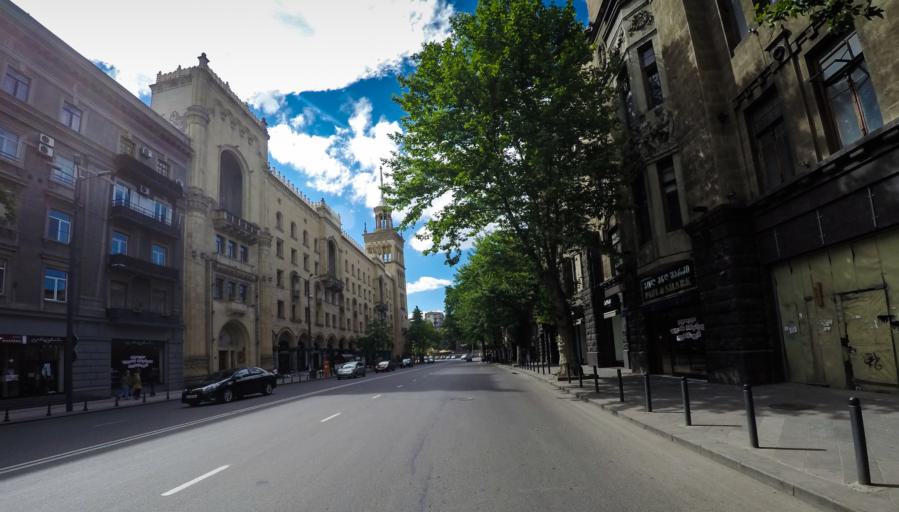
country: GE
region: T'bilisi
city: Tbilisi
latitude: 41.7031
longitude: 44.7918
